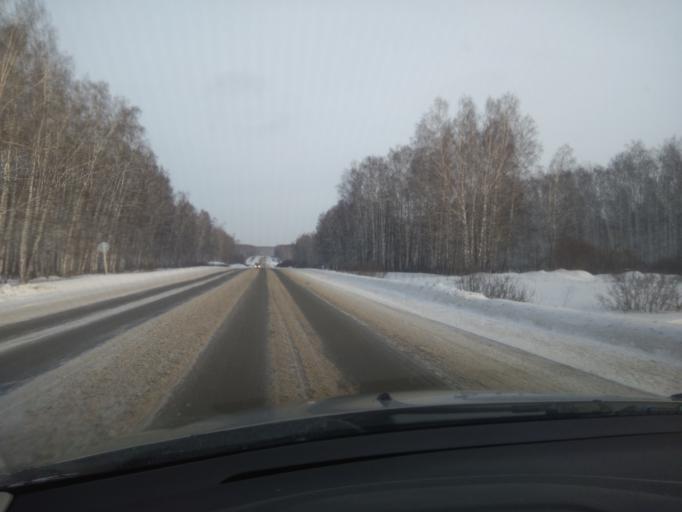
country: RU
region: Sverdlovsk
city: Bogdanovich
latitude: 56.7835
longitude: 61.9979
